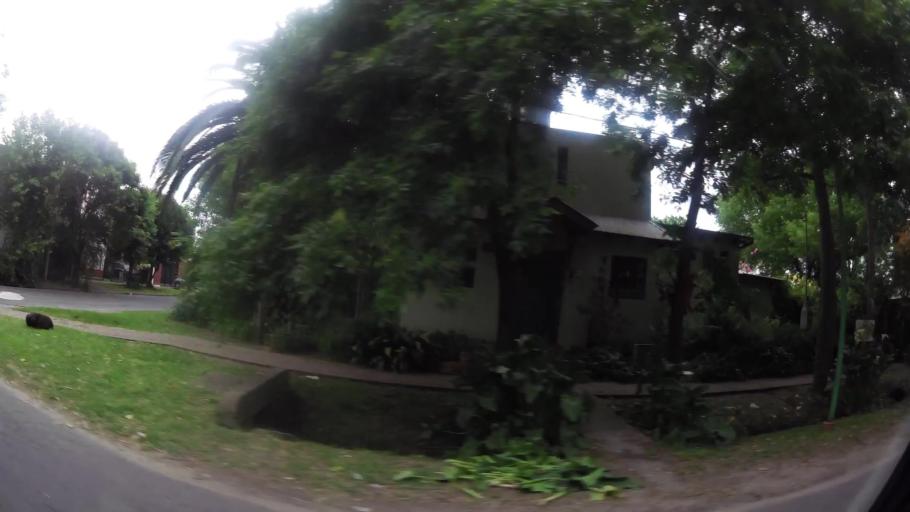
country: AR
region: Buenos Aires
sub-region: Partido de La Plata
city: La Plata
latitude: -34.9341
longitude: -57.9889
